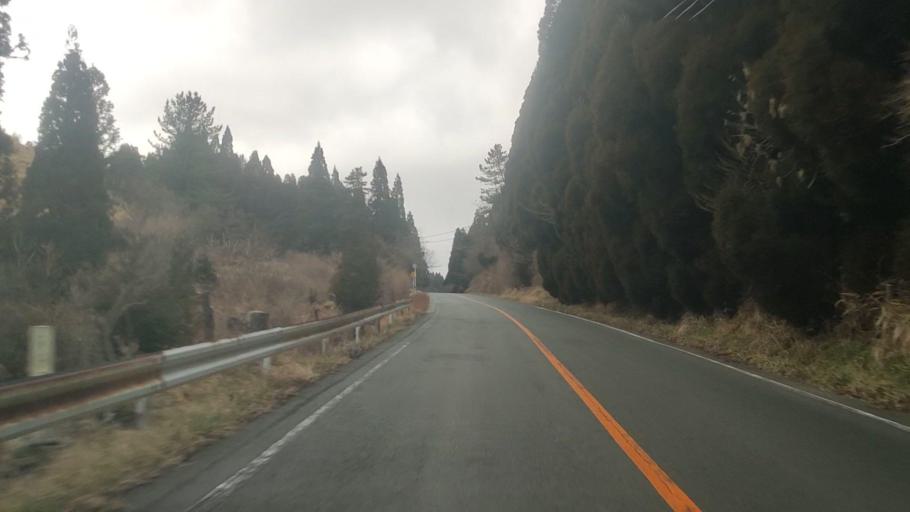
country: JP
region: Kumamoto
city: Aso
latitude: 32.8880
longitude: 131.1693
